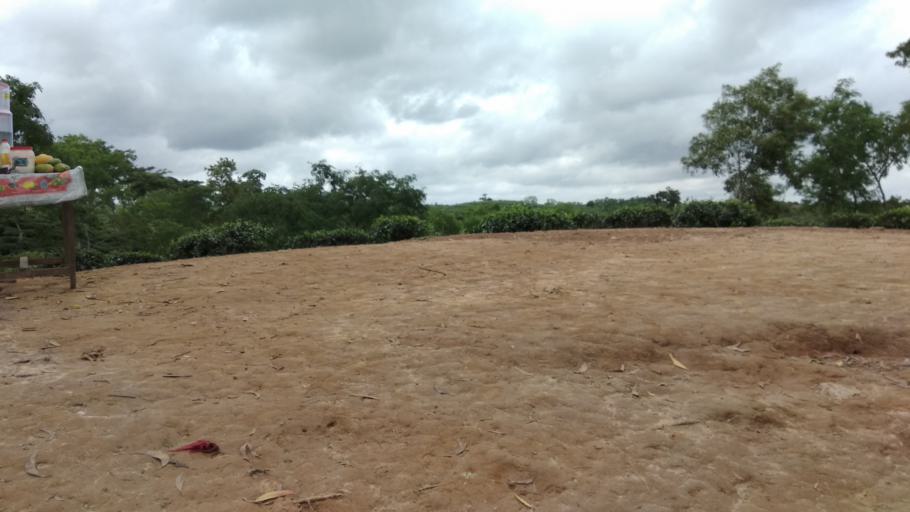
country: IN
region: Tripura
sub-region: Dhalai
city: Kamalpur
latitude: 24.2811
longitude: 91.8206
